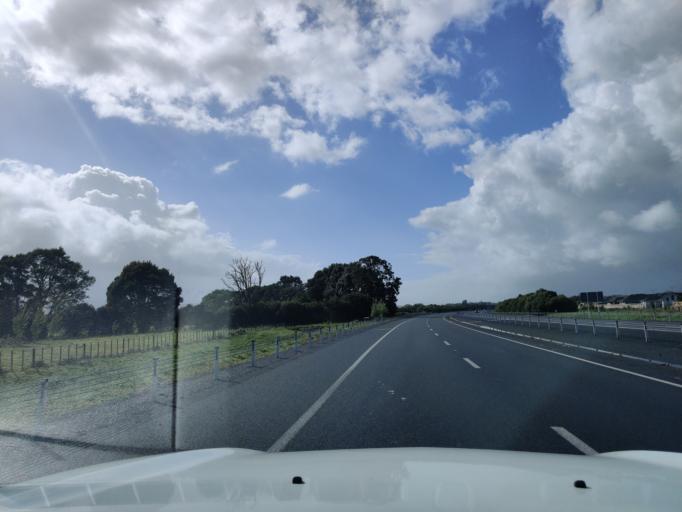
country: NZ
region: Waikato
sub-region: Waipa District
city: Cambridge
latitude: -37.8711
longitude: 175.4770
